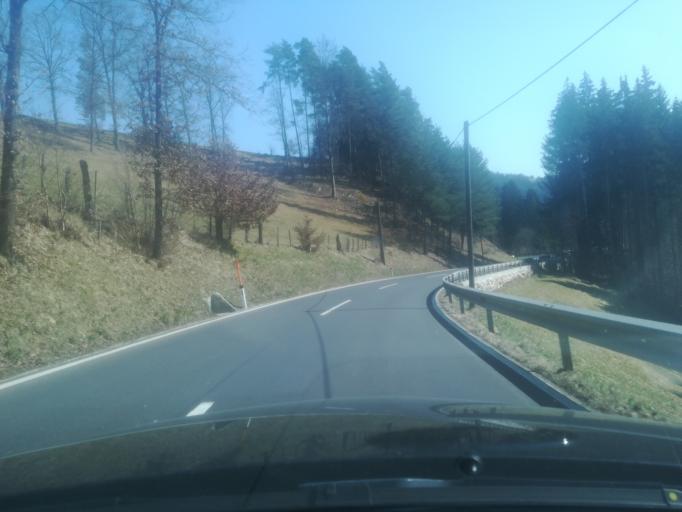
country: AT
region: Upper Austria
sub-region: Politischer Bezirk Freistadt
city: Freistadt
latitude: 48.4184
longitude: 14.6311
